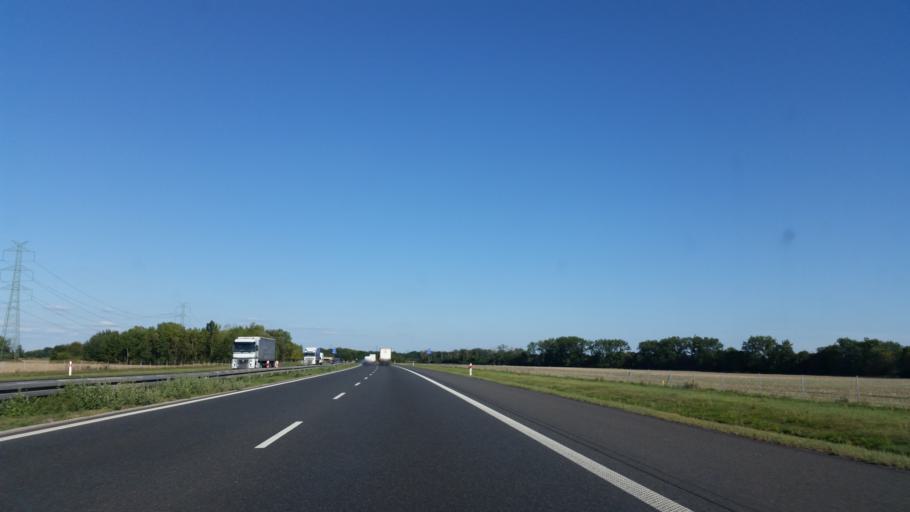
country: PL
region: Opole Voivodeship
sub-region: Powiat brzeski
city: Grodkow
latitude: 50.7711
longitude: 17.3781
